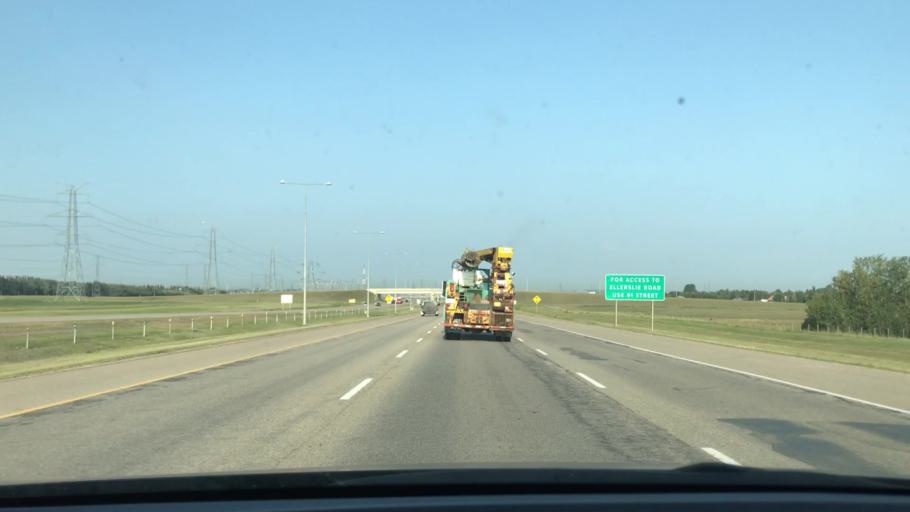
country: CA
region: Alberta
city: Beaumont
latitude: 53.4358
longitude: -113.4320
